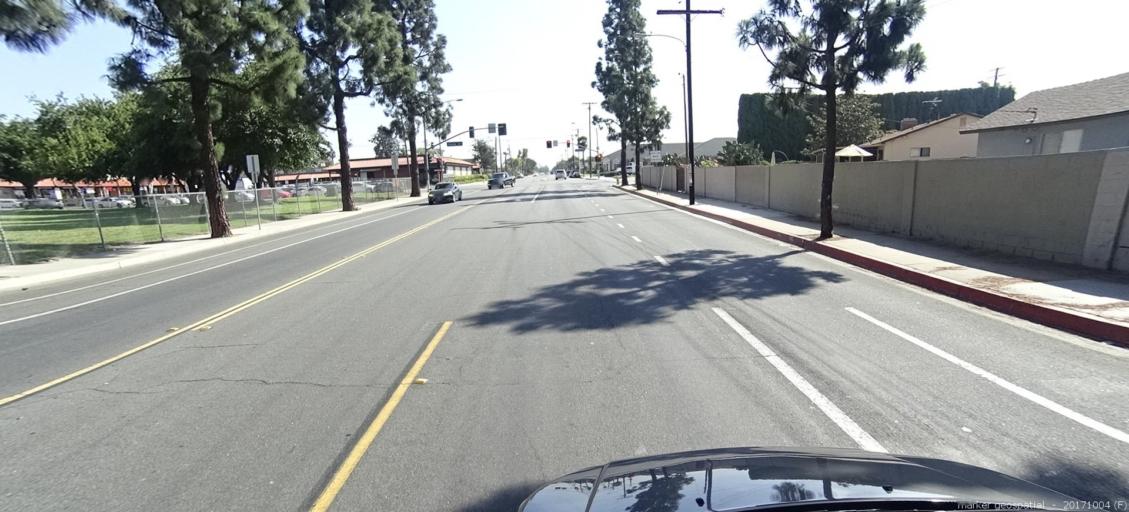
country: US
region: California
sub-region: Orange County
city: Garden Grove
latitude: 33.7959
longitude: -117.9422
